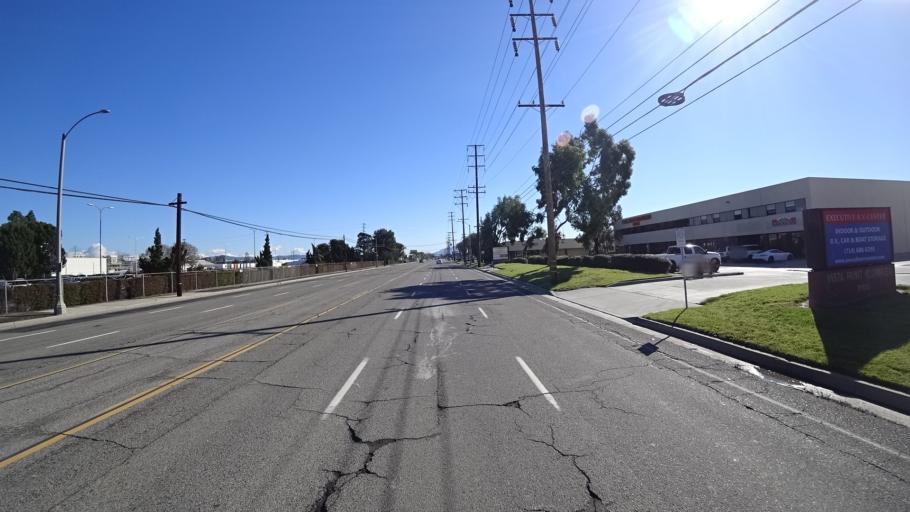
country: US
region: California
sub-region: Orange County
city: Placentia
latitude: 33.8596
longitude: -117.8945
